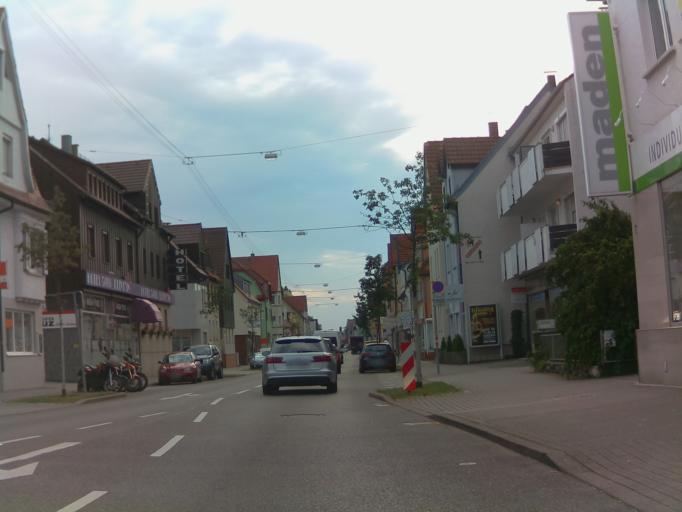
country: DE
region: Baden-Wuerttemberg
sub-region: Regierungsbezirk Stuttgart
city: Steinenbronn
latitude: 48.7299
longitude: 9.1033
